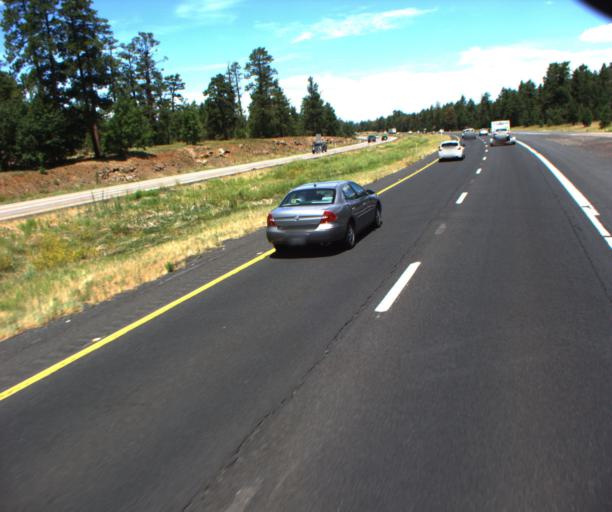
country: US
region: Arizona
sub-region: Coconino County
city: Sedona
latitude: 34.8552
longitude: -111.6081
